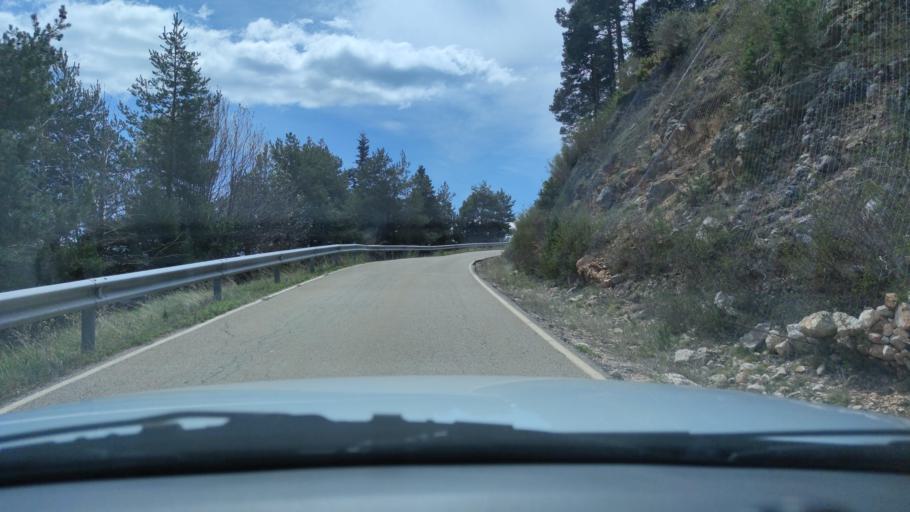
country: ES
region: Catalonia
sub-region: Provincia de Lleida
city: Gosol
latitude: 42.1987
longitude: 1.5640
